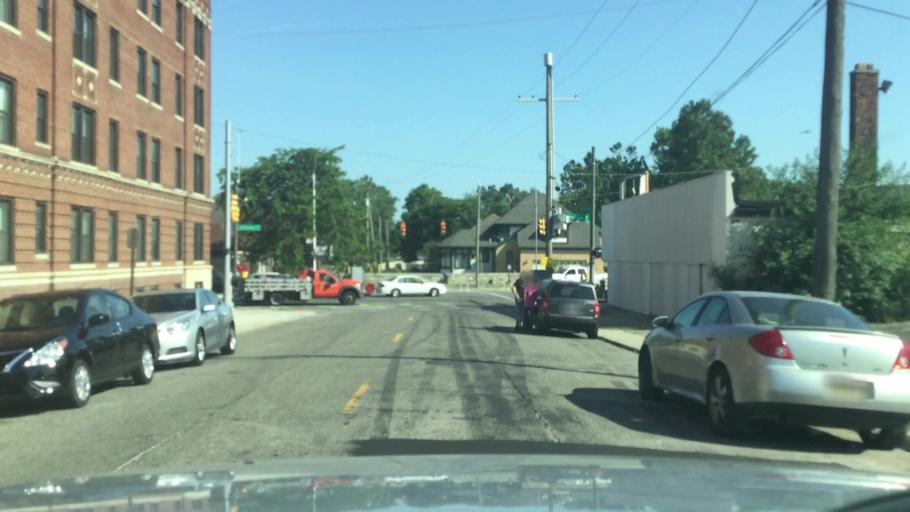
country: US
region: Michigan
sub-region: Wayne County
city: Grosse Pointe Park
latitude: 42.3594
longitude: -82.9850
